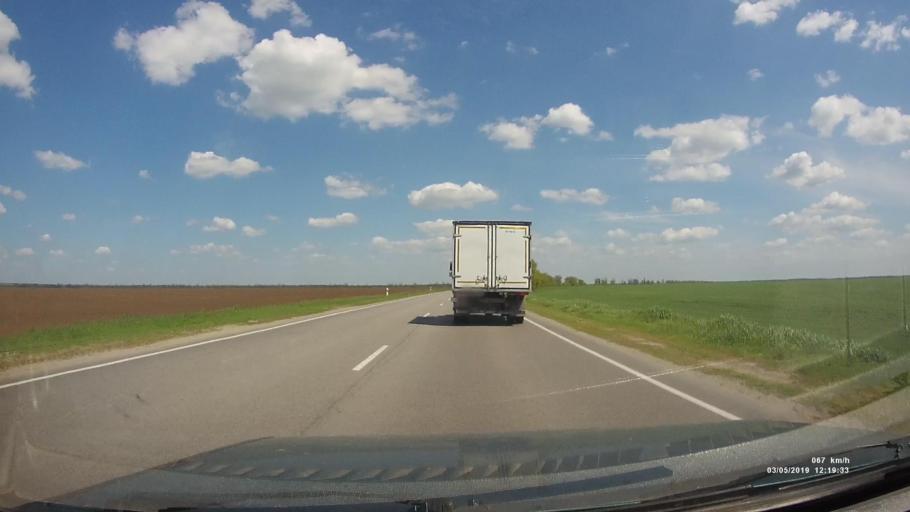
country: RU
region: Rostov
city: Melikhovskaya
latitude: 47.4012
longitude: 40.6094
